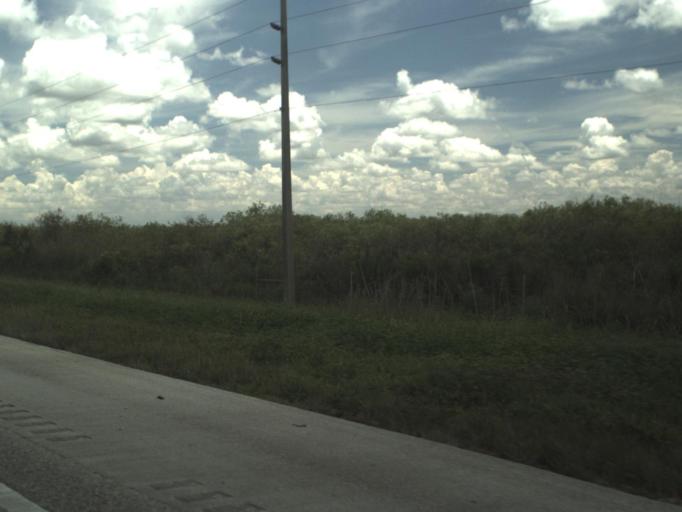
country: US
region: Florida
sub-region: Broward County
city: Weston
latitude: 26.1592
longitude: -80.7827
